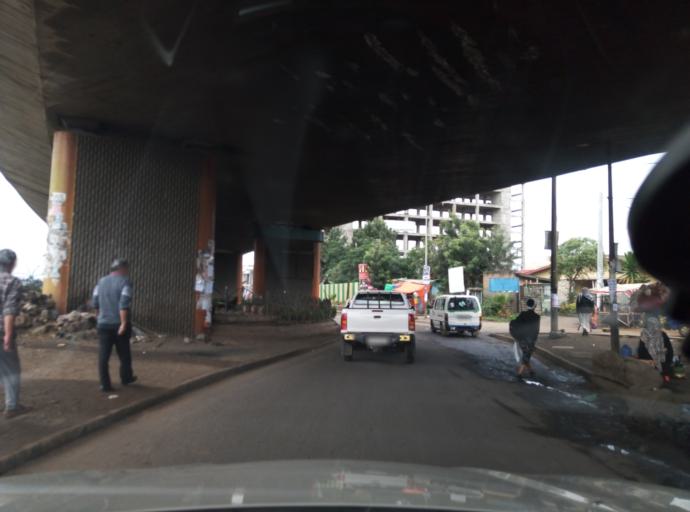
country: ET
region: Adis Abeba
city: Addis Ababa
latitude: 9.0108
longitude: 38.7210
